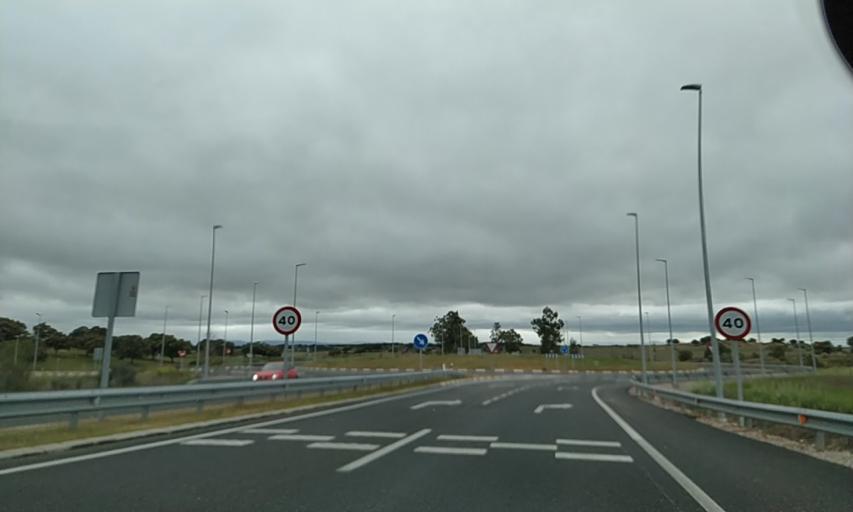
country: ES
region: Extremadura
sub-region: Provincia de Caceres
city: Caceres
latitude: 39.4658
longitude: -6.4059
